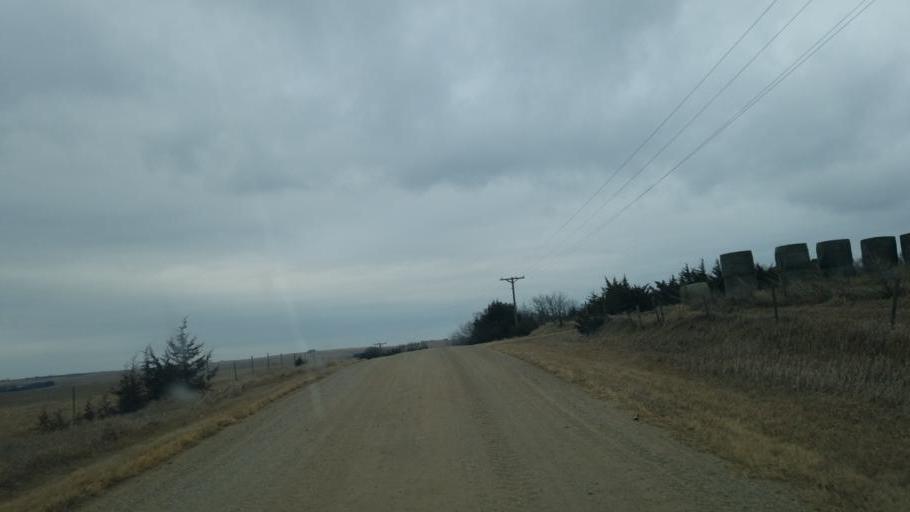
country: US
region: South Dakota
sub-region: Yankton County
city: Yankton
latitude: 42.7577
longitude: -97.3913
